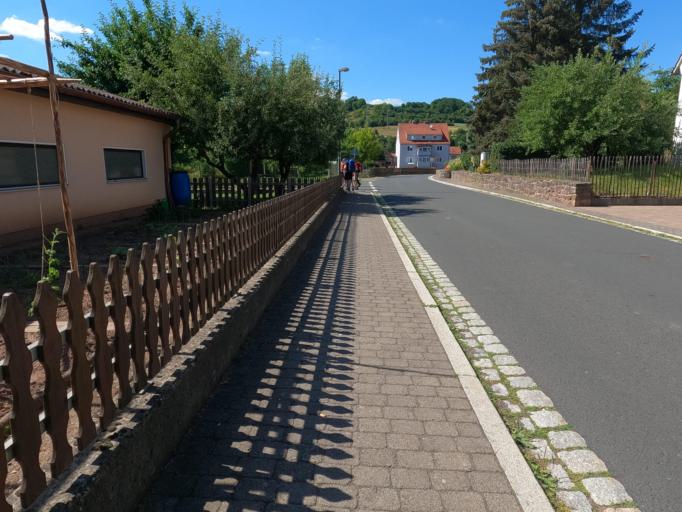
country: DE
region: Hesse
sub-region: Regierungsbezirk Darmstadt
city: Schluchtern
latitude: 50.3584
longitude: 9.5574
